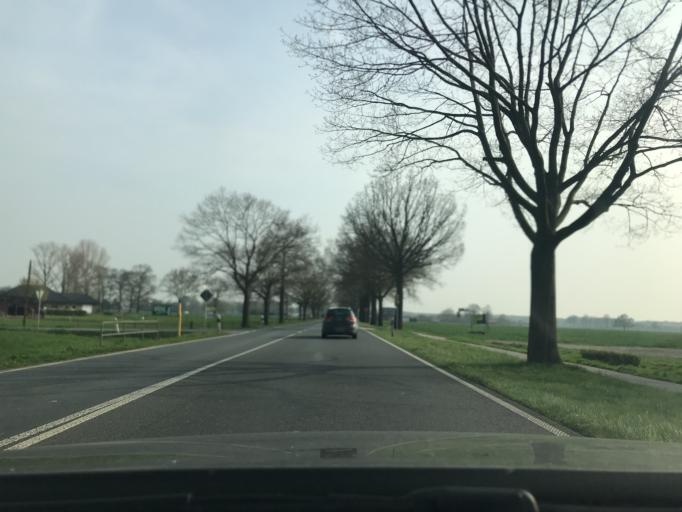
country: DE
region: North Rhine-Westphalia
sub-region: Regierungsbezirk Dusseldorf
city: Kevelaer
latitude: 51.5498
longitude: 6.2668
